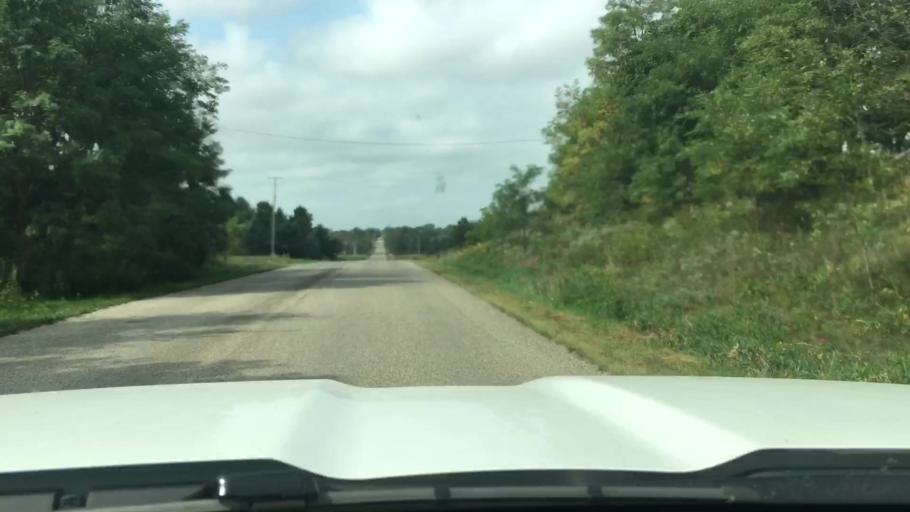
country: US
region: Michigan
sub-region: Eaton County
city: Potterville
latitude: 42.6256
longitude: -84.6924
